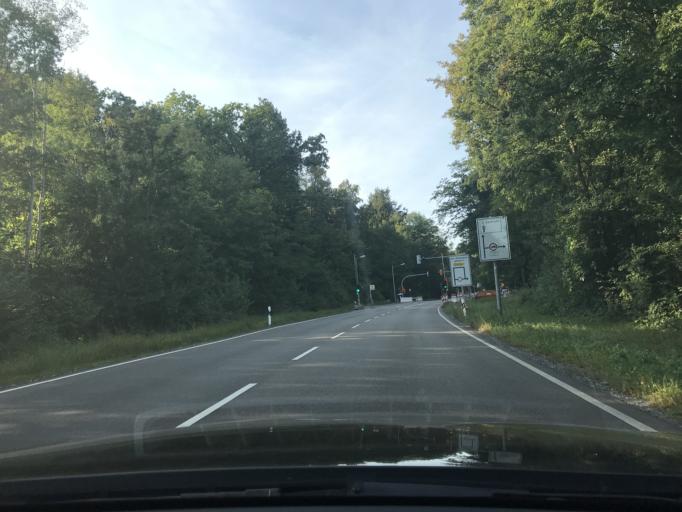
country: DE
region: Baden-Wuerttemberg
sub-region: Regierungsbezirk Stuttgart
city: Stuttgart-Ost
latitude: 48.7437
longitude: 9.2005
